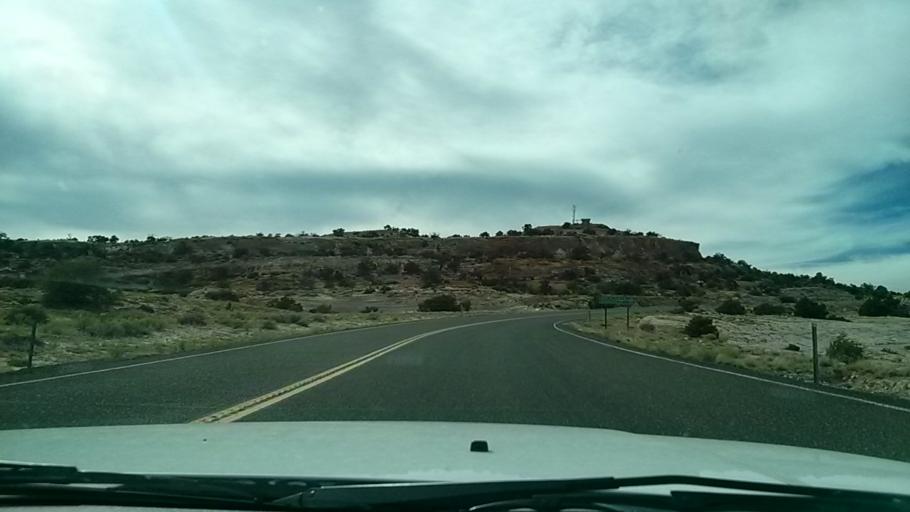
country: US
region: Utah
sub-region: Wayne County
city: Loa
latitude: 37.7474
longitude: -111.4549
